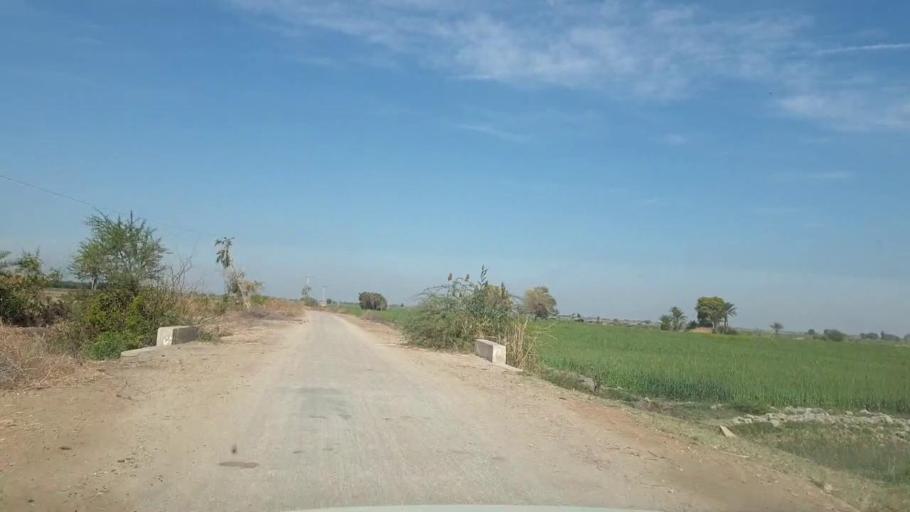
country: PK
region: Sindh
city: Mirpur Khas
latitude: 25.6353
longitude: 69.1963
